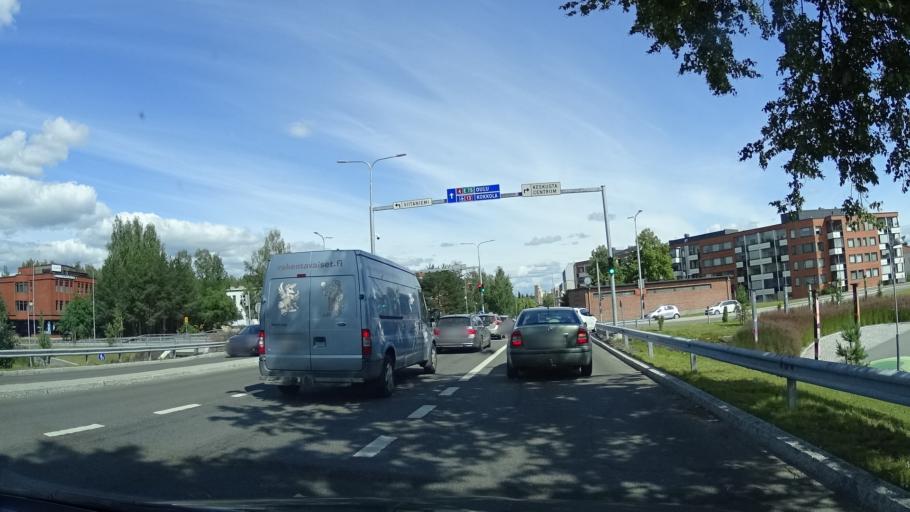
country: FI
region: Central Finland
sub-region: Jyvaeskylae
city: Jyvaeskylae
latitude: 62.2481
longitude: 25.7382
